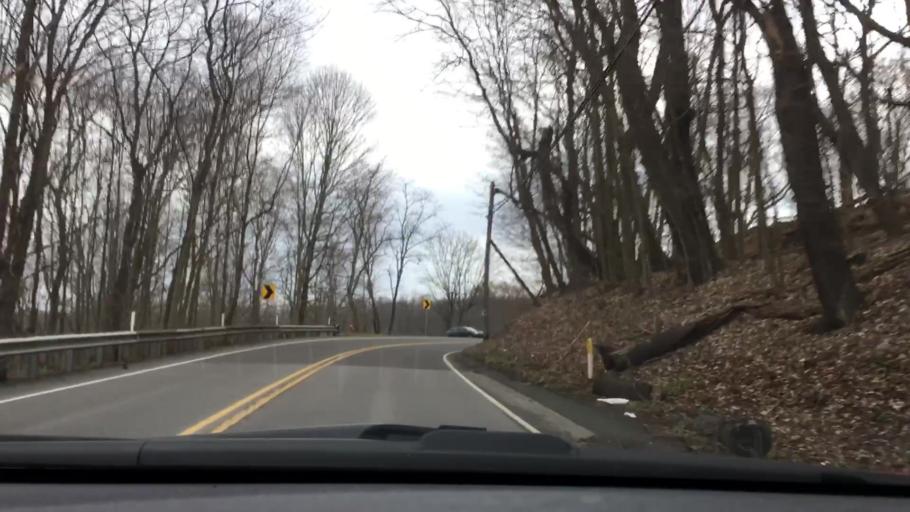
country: US
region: Pennsylvania
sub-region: Washington County
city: Cecil-Bishop
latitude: 40.3191
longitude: -80.2302
